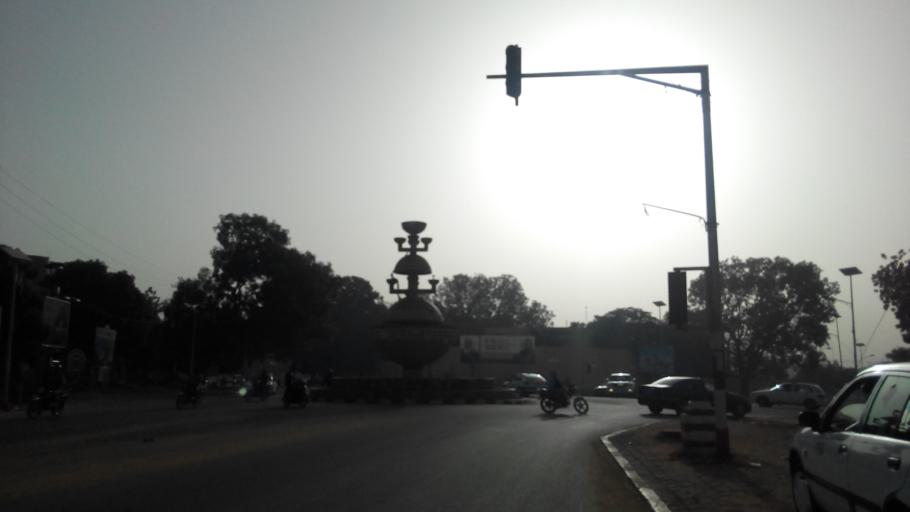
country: NE
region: Niamey
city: Niamey
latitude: 13.5153
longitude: 2.1009
